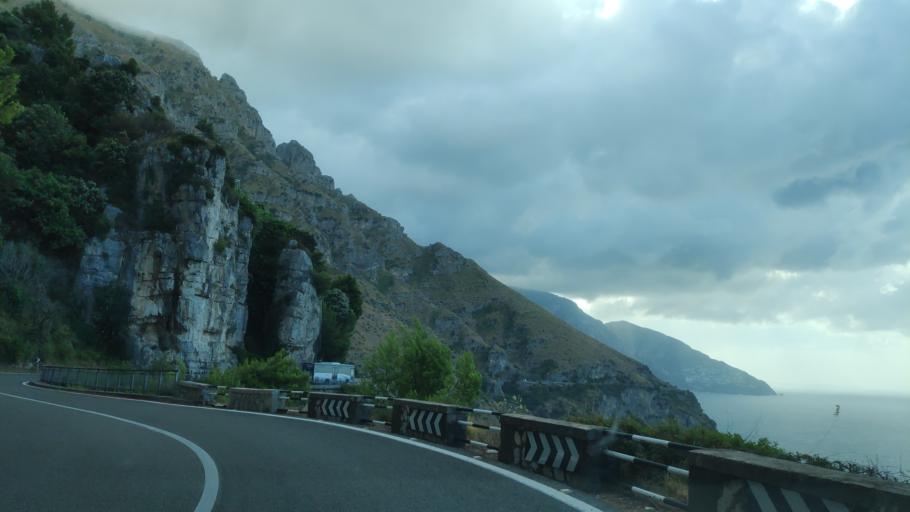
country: IT
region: Campania
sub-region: Provincia di Napoli
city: Arola-Preazzano
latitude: 40.6192
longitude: 14.4482
